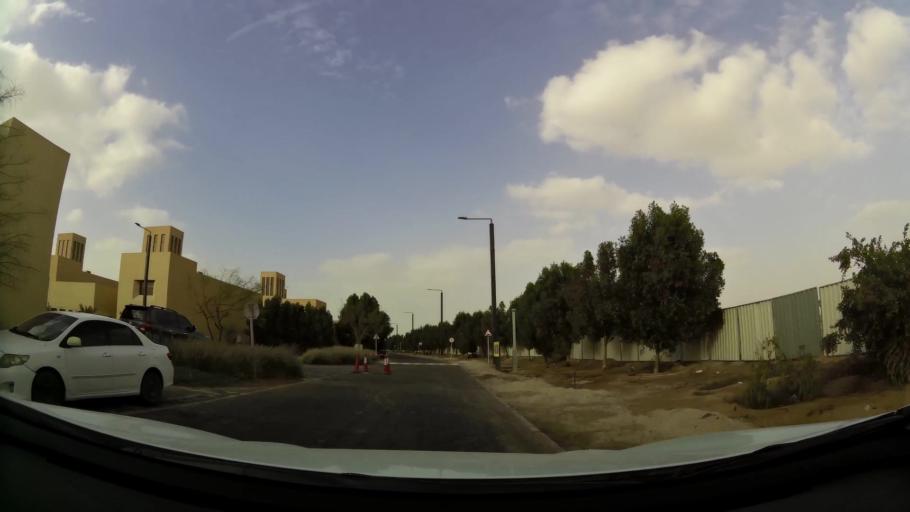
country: AE
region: Abu Dhabi
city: Abu Dhabi
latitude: 24.4997
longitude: 54.6027
